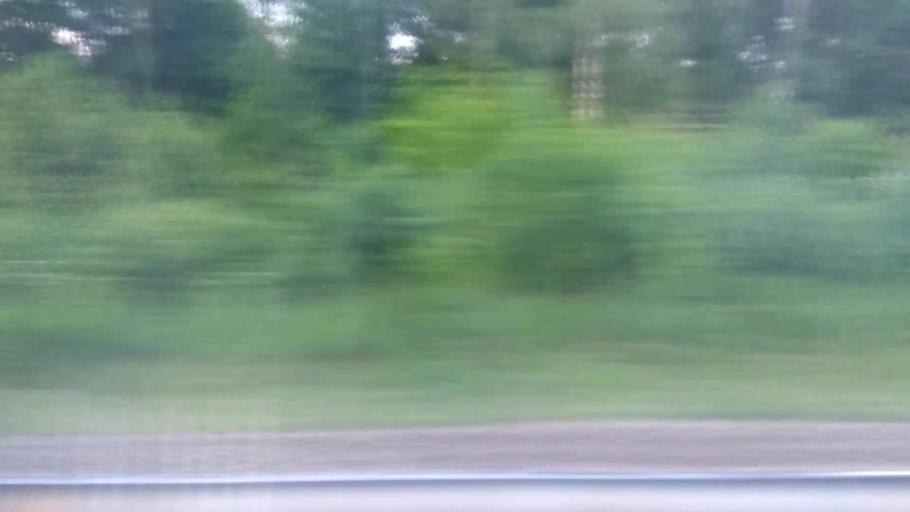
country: RU
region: Moskovskaya
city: Vostryakovo
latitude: 55.4105
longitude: 37.7938
